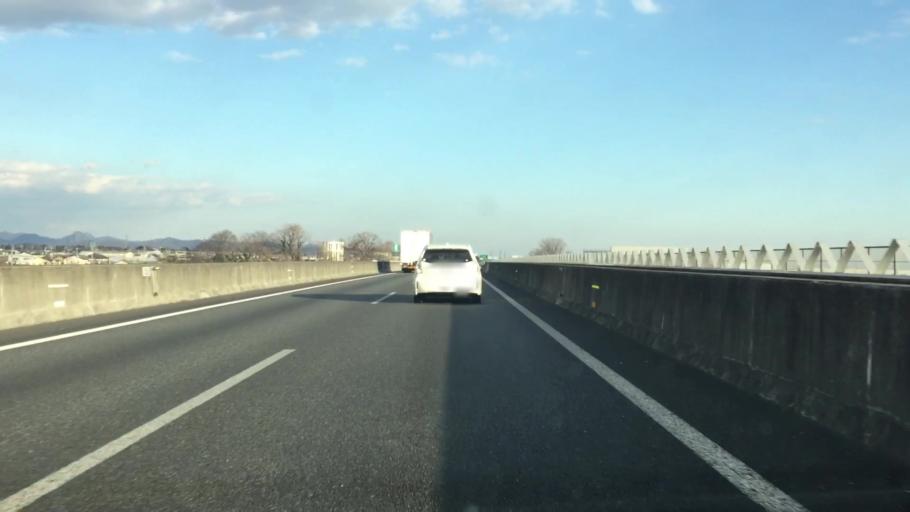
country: JP
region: Gunma
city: Isesaki
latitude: 36.3559
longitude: 139.2096
